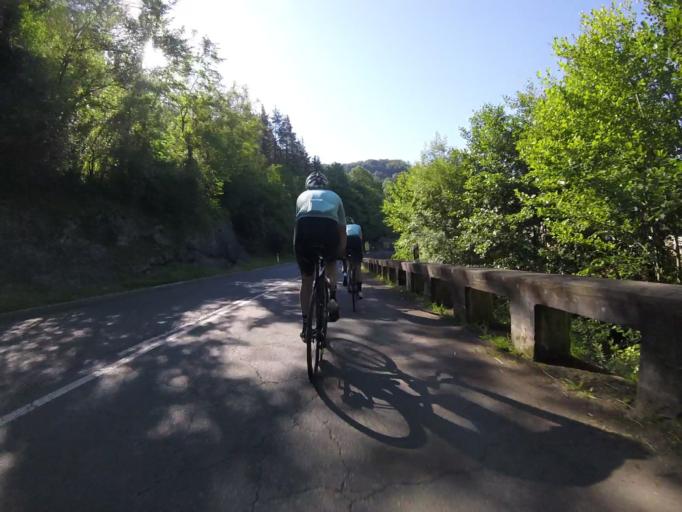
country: ES
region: Basque Country
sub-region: Provincia de Guipuzcoa
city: Beizama
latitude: 43.1470
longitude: -2.2329
